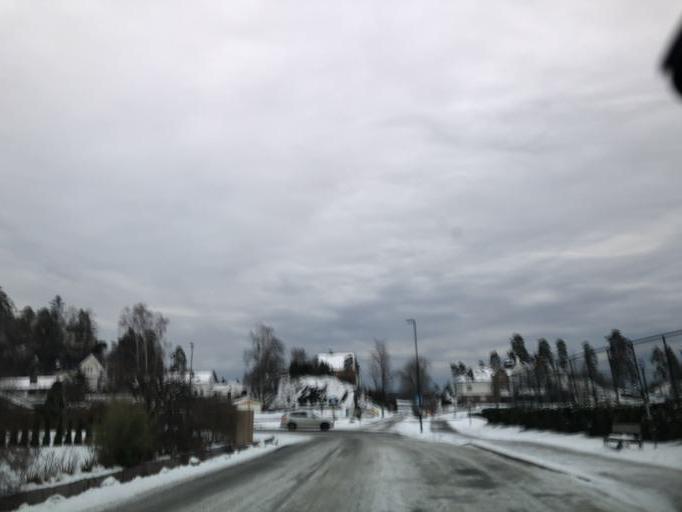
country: NO
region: Akershus
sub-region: Baerum
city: Sandvika
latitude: 59.8598
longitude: 10.5169
